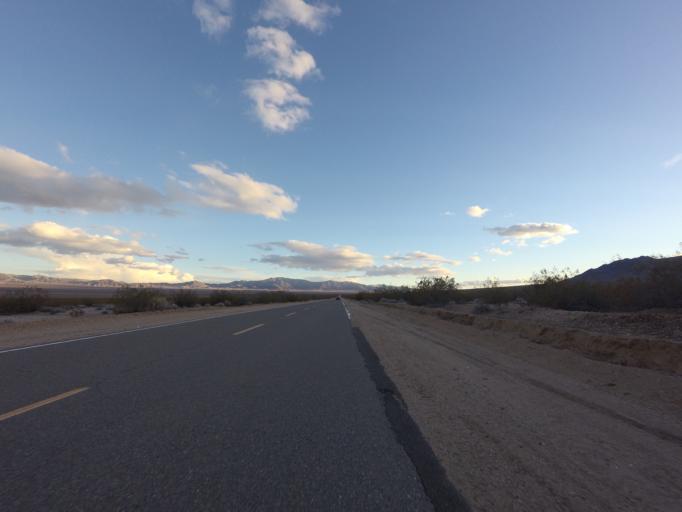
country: US
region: Nevada
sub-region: Clark County
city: Sandy Valley
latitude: 35.4551
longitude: -115.3893
